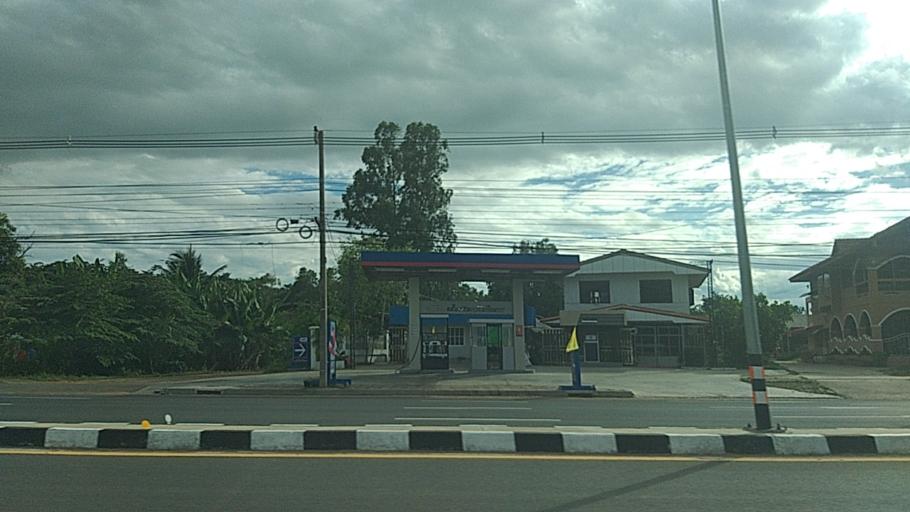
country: TH
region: Surin
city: Prasat
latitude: 14.6141
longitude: 103.4172
